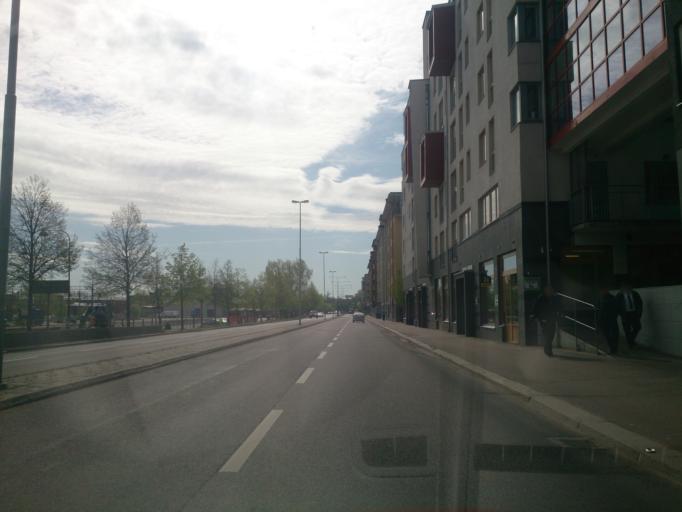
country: SE
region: OEstergoetland
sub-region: Linkopings Kommun
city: Linkoping
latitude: 58.4189
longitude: 15.6193
